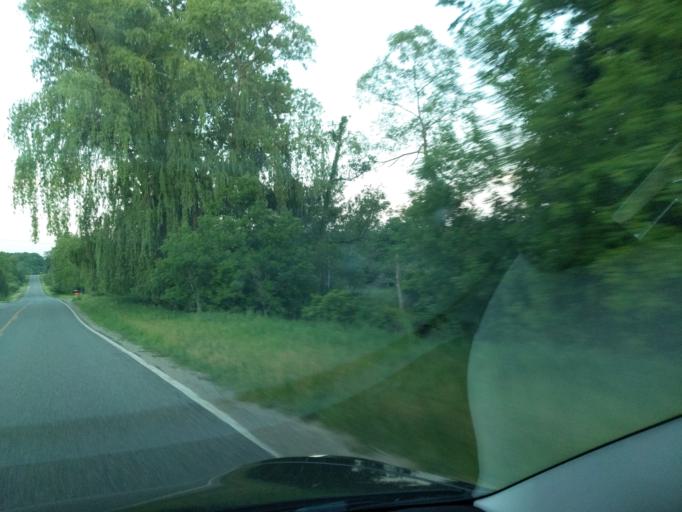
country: US
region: Michigan
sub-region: Barry County
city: Nashville
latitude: 42.5380
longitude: -85.1045
